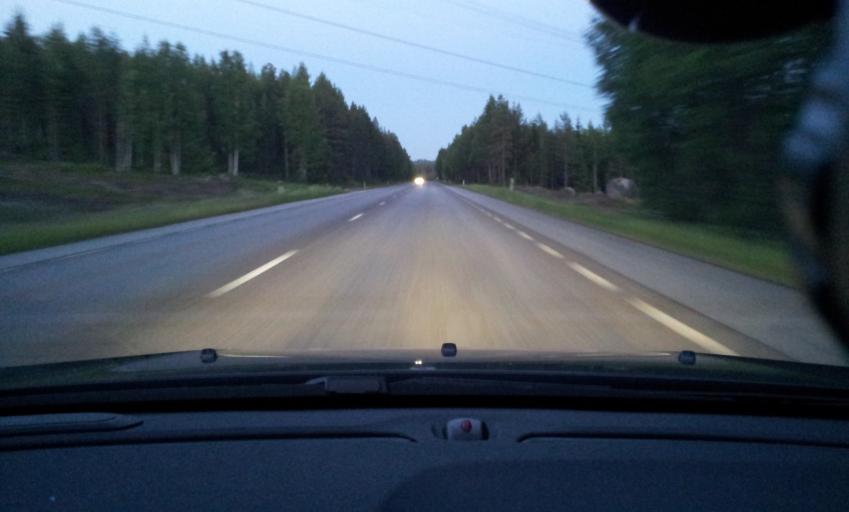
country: SE
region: Jaemtland
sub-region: Braecke Kommun
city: Braecke
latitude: 62.7244
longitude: 15.4447
